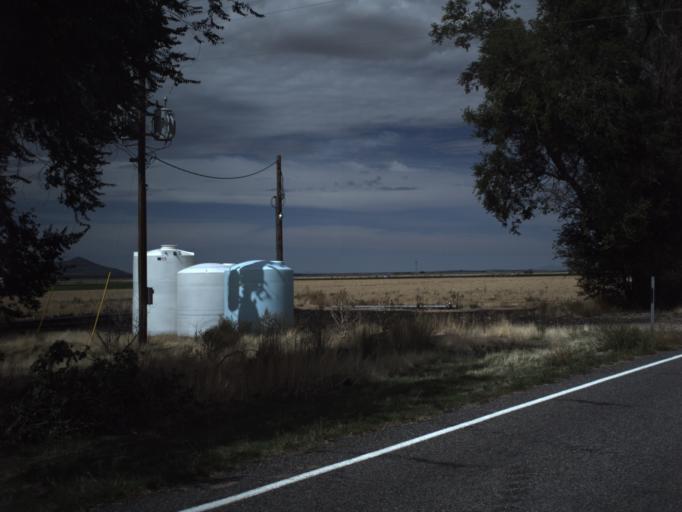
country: US
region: Utah
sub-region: Millard County
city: Fillmore
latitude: 39.0483
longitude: -112.4098
